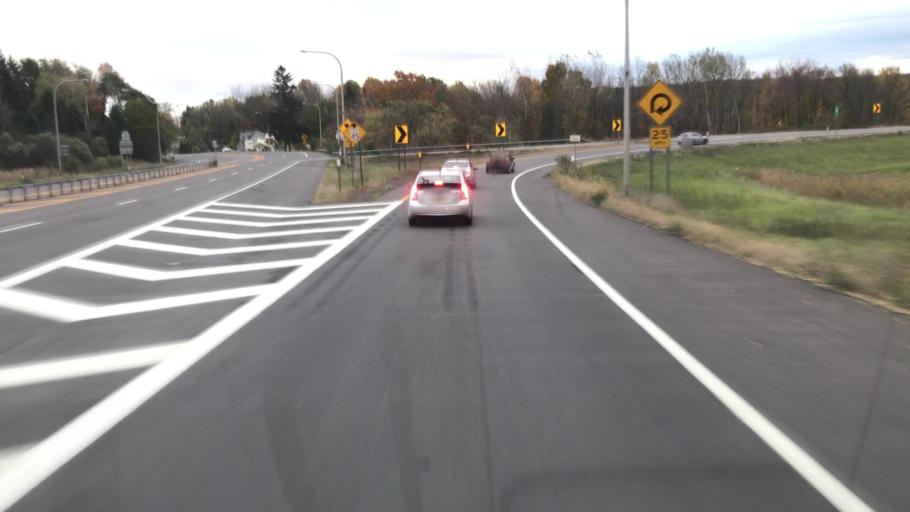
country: US
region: New York
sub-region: Onondaga County
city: Camillus
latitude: 43.0348
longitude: -76.3225
